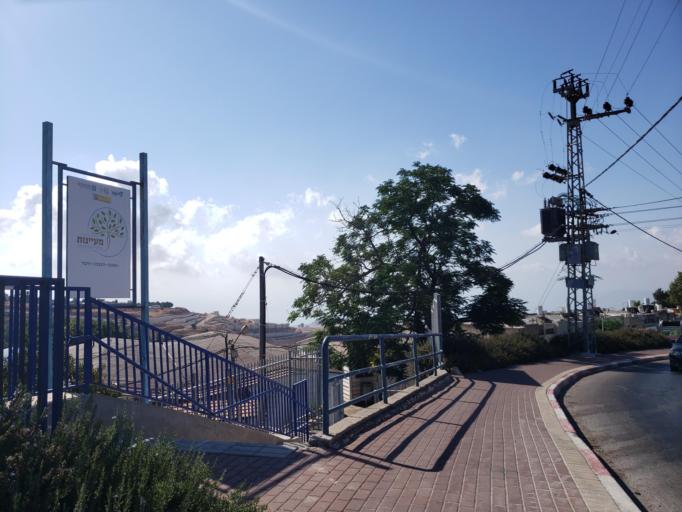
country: IL
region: Northern District
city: Safed
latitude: 32.9632
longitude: 35.4990
